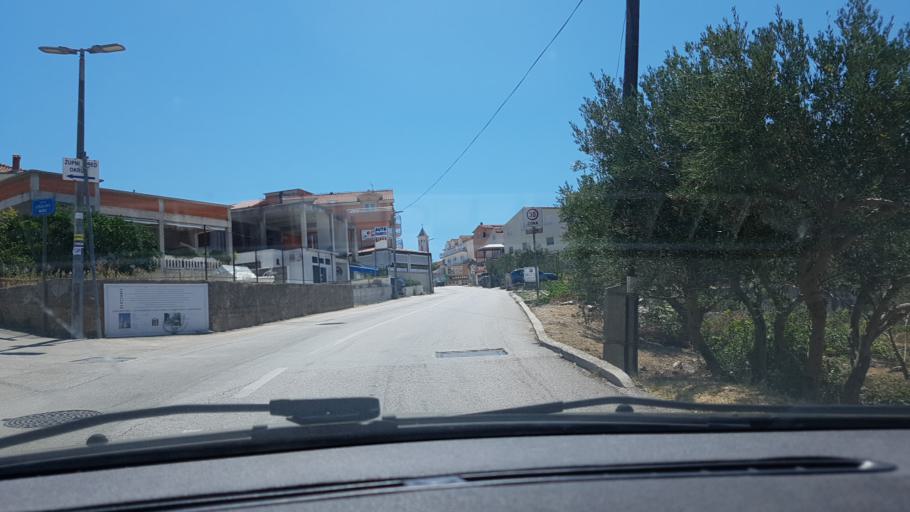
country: HR
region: Splitsko-Dalmatinska
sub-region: Grad Trogir
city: Trogir
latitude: 43.4950
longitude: 16.2632
